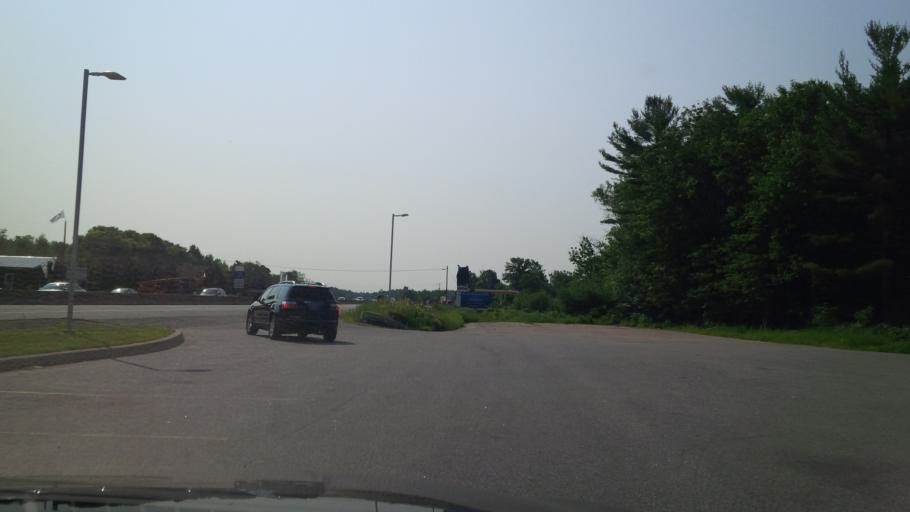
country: CA
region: Ontario
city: Gravenhurst
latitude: 44.8846
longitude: -79.3469
